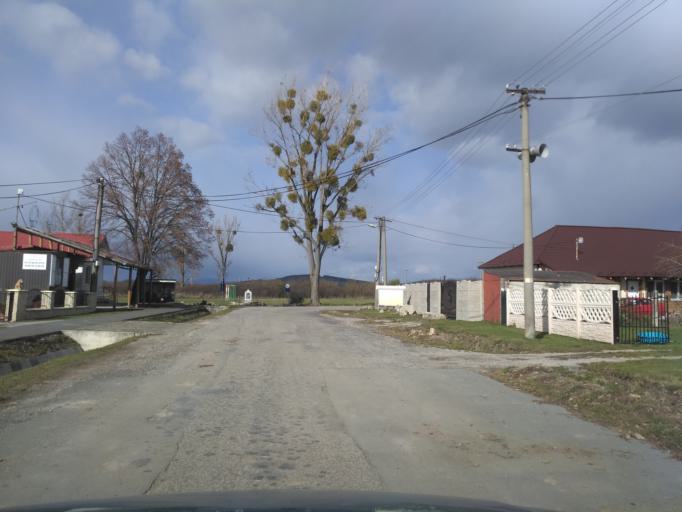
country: HU
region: Borsod-Abauj-Zemplen
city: Satoraljaujhely
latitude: 48.4241
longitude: 21.6760
